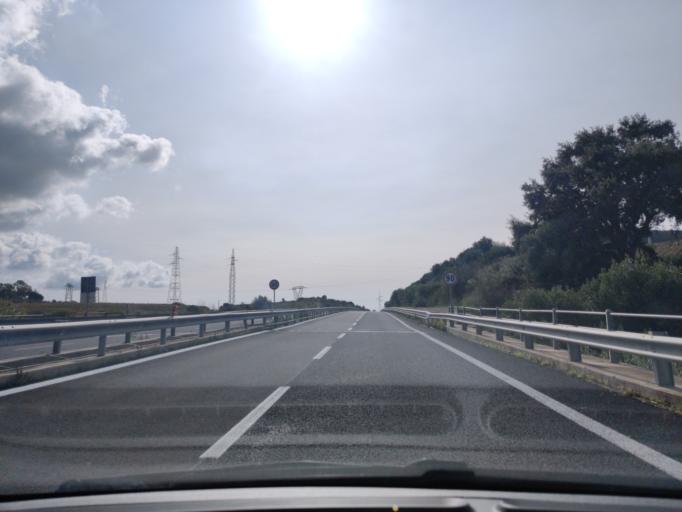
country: IT
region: Latium
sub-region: Citta metropolitana di Roma Capitale
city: Aurelia
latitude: 42.1174
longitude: 11.7916
